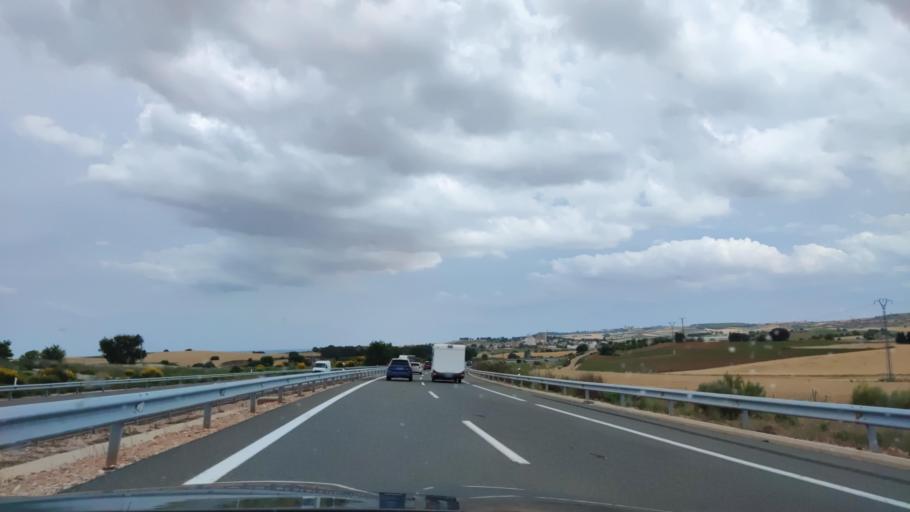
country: ES
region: Castille-La Mancha
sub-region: Provincia de Cuenca
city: Castillo de Garcimunoz
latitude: 39.7044
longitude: -2.3884
